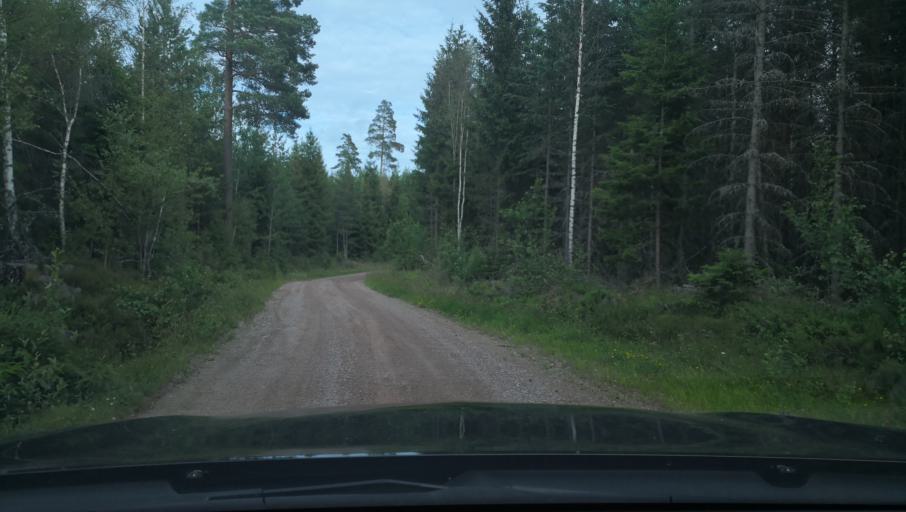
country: SE
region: Vaestmanland
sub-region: Surahammars Kommun
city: Surahammar
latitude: 59.6583
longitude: 16.1327
